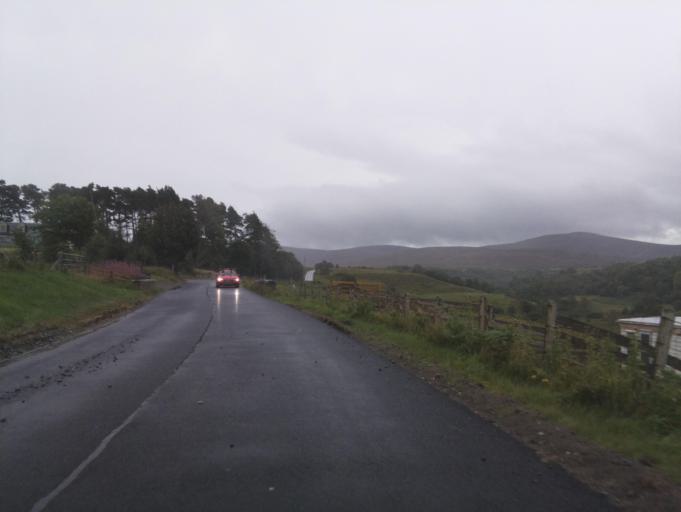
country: GB
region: Scotland
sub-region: Highland
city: Grantown on Spey
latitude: 57.3042
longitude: -3.5705
